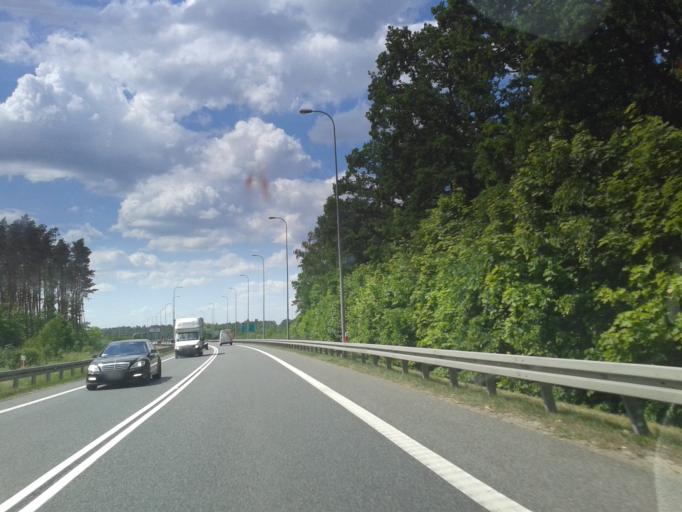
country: PL
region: Pomeranian Voivodeship
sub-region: Powiat chojnicki
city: Chojnice
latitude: 53.7108
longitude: 17.6487
